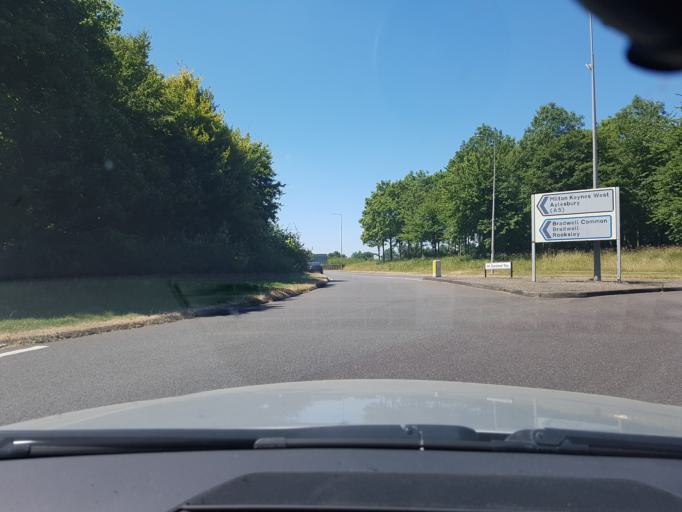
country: GB
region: England
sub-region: Milton Keynes
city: Milton Keynes
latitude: 52.0499
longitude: -0.7668
